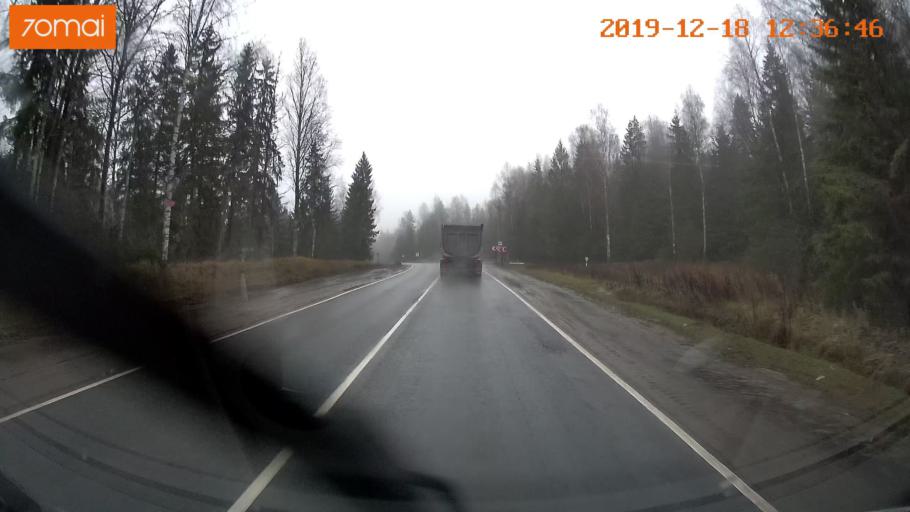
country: RU
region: Moskovskaya
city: Rumyantsevo
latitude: 56.1392
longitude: 36.5965
